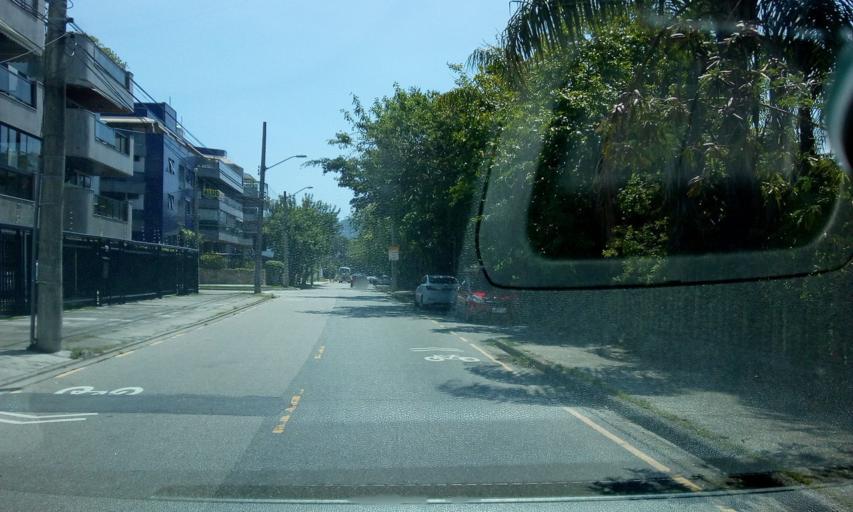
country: BR
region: Rio de Janeiro
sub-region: Nilopolis
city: Nilopolis
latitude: -23.0222
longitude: -43.4557
